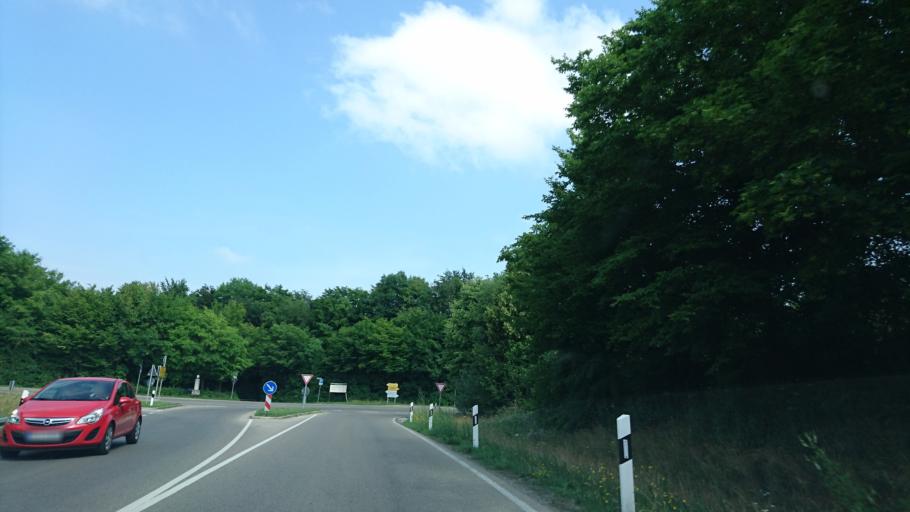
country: DE
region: Bavaria
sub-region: Swabia
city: Stadtbergen
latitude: 48.3710
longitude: 10.8160
